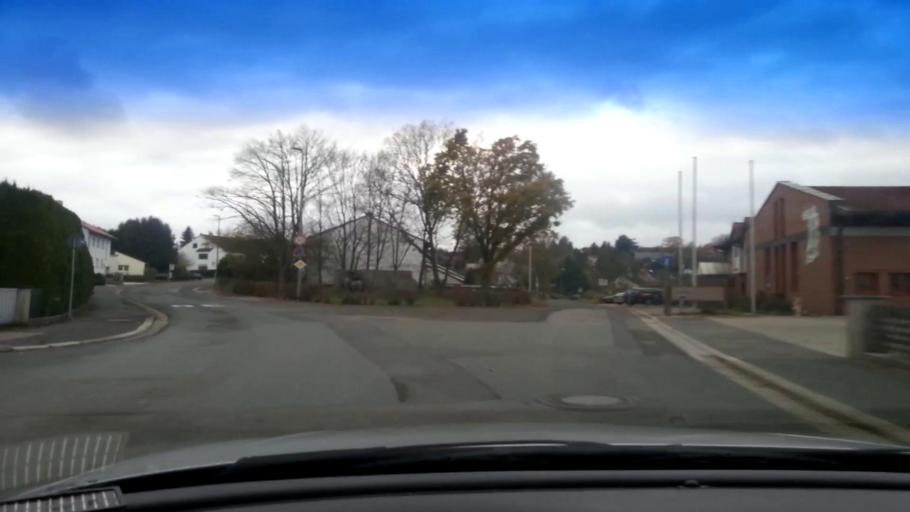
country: DE
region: Bavaria
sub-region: Upper Franconia
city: Stegaurach
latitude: 49.8609
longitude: 10.8385
